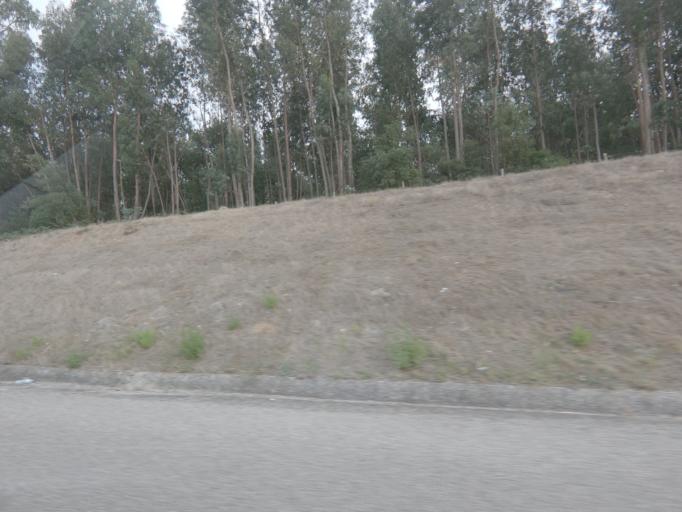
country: PT
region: Coimbra
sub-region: Coimbra
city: Coimbra
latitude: 40.2058
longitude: -8.4485
